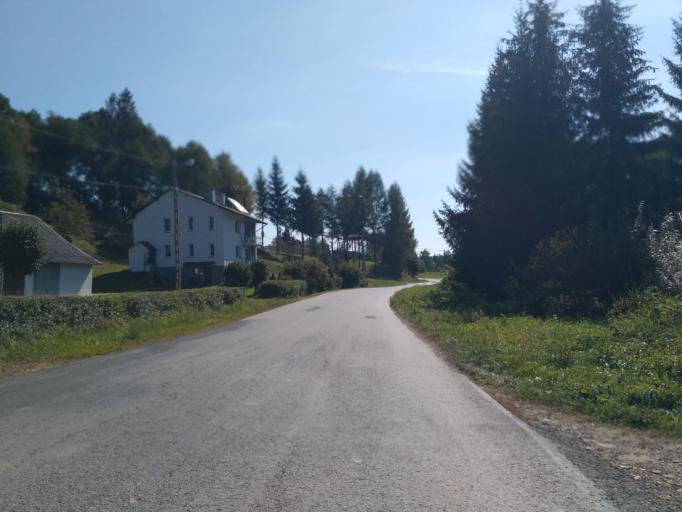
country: PL
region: Subcarpathian Voivodeship
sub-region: Powiat brzozowski
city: Niebocko
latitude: 49.6588
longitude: 22.1334
